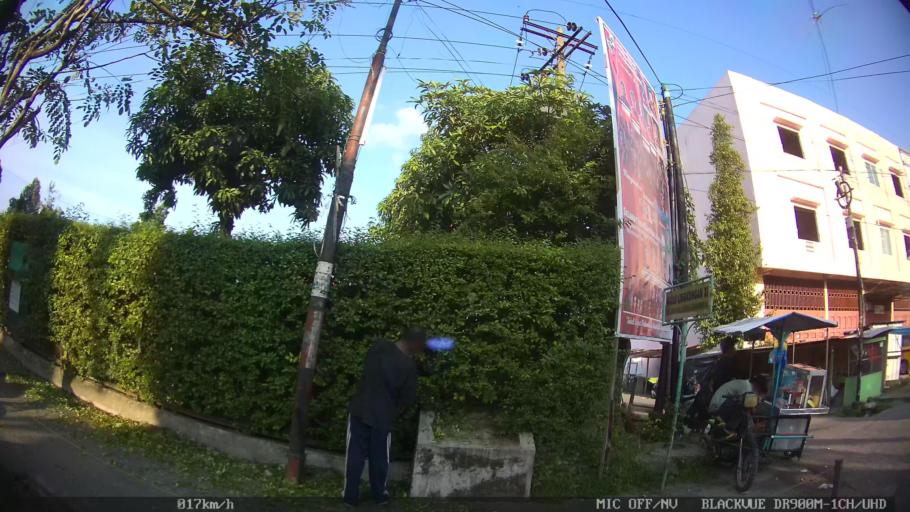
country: ID
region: North Sumatra
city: Medan
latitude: 3.6135
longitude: 98.6657
